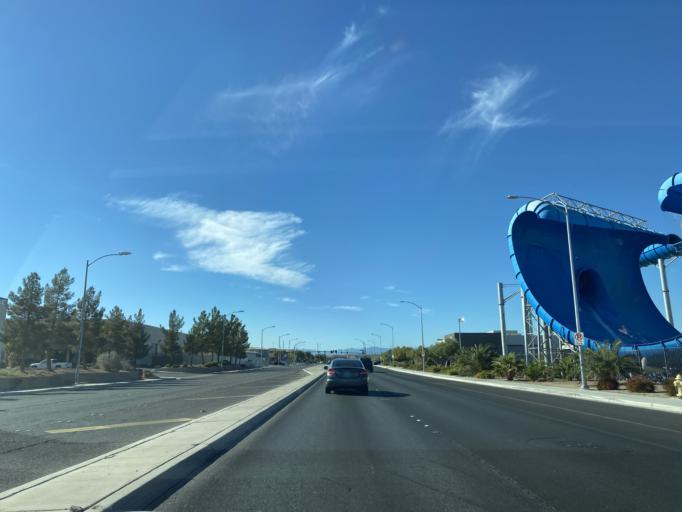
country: US
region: Nevada
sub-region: Clark County
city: Henderson
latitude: 36.0710
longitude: -115.0251
